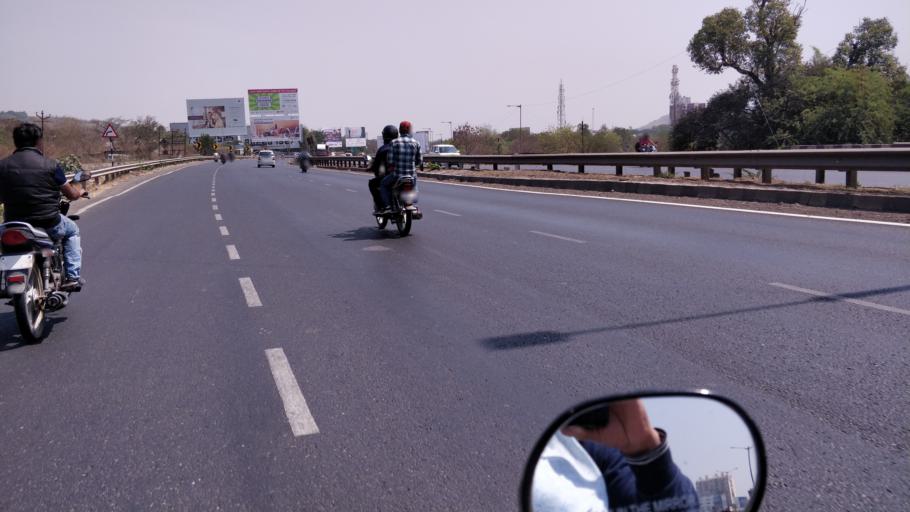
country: IN
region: Maharashtra
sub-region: Pune Division
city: Shivaji Nagar
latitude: 18.5246
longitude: 73.7715
